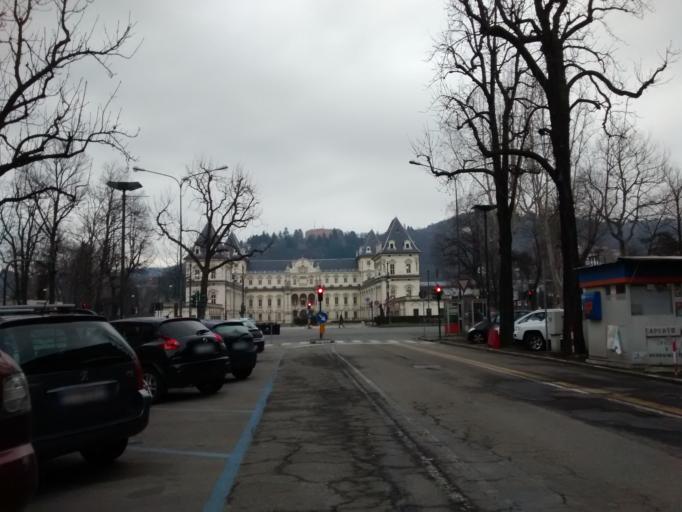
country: IT
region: Piedmont
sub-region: Provincia di Torino
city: Turin
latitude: 45.0550
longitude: 7.6838
